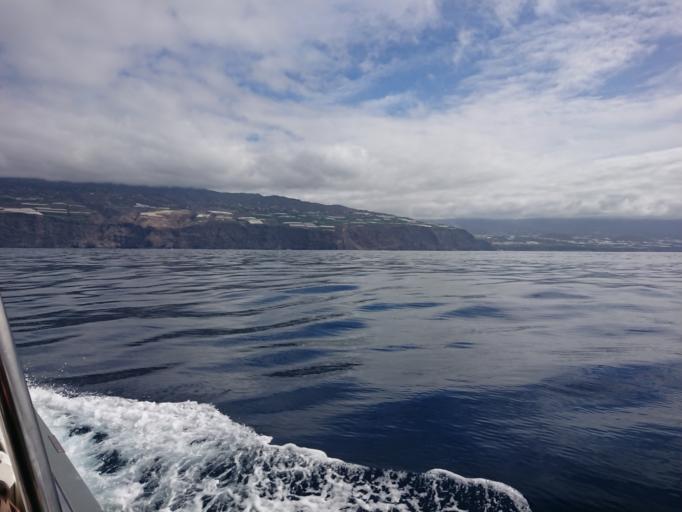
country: ES
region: Canary Islands
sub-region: Provincia de Santa Cruz de Tenerife
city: Tijarafe
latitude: 28.6701
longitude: -18.0062
